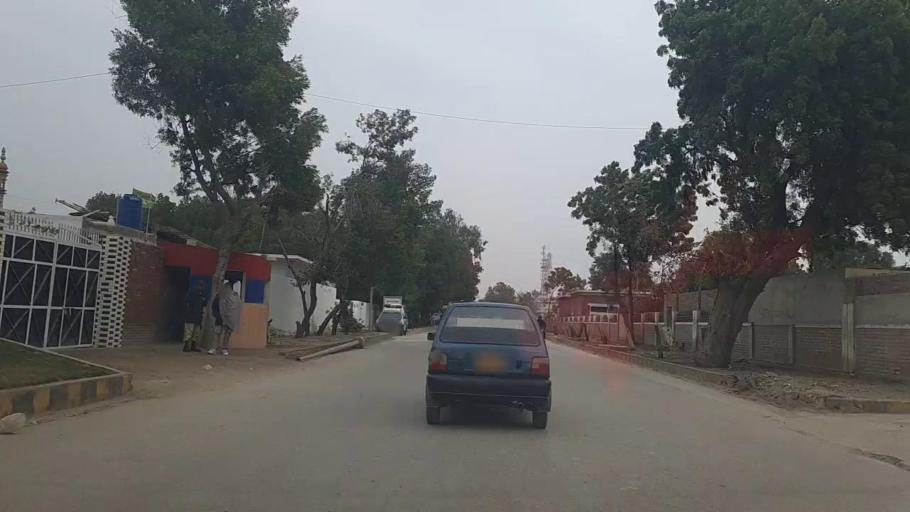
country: PK
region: Sindh
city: Nawabshah
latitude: 26.2487
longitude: 68.4021
